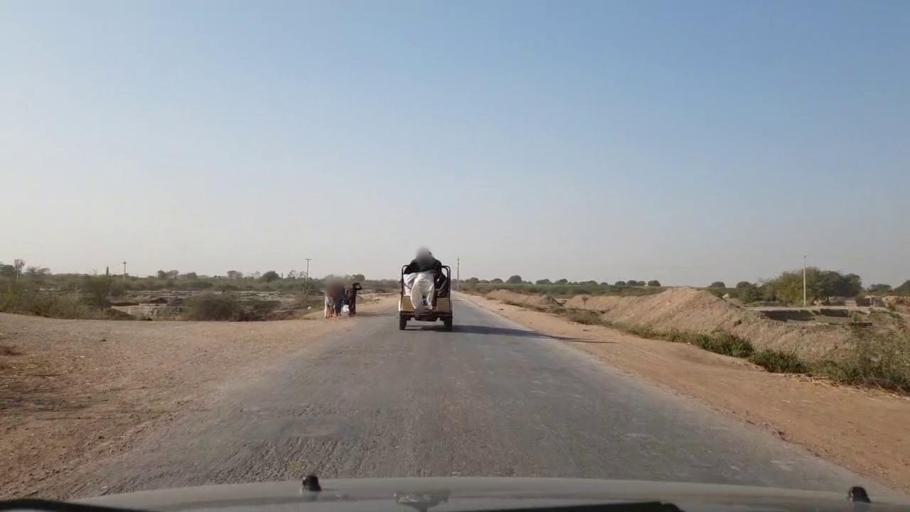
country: PK
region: Sindh
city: Tando Ghulam Ali
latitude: 25.1429
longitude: 68.8695
